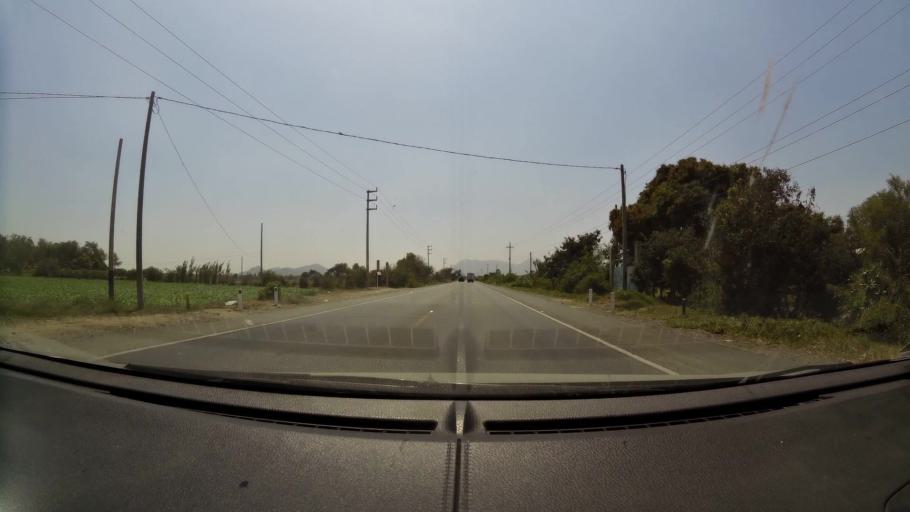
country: PE
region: Lambayeque
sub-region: Provincia de Chiclayo
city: Mocupe
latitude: -7.0073
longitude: -79.6125
